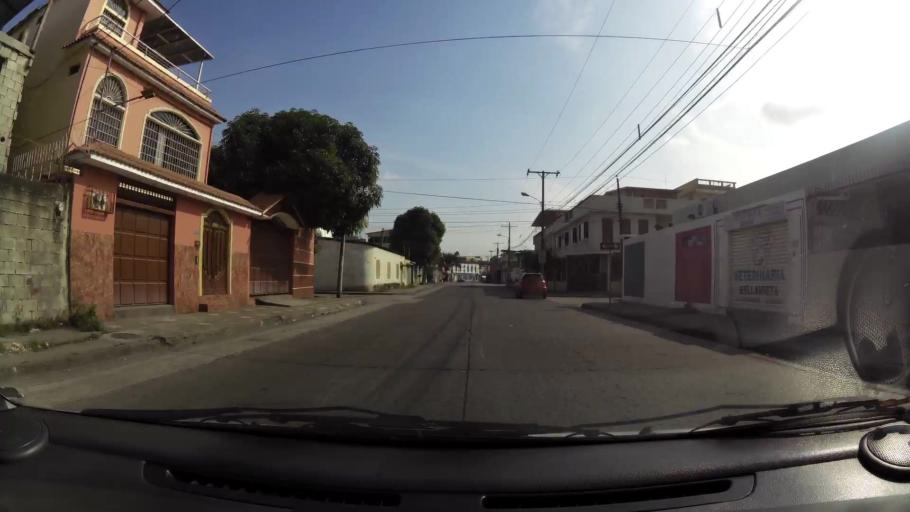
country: EC
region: Guayas
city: Guayaquil
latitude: -2.1843
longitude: -79.9101
